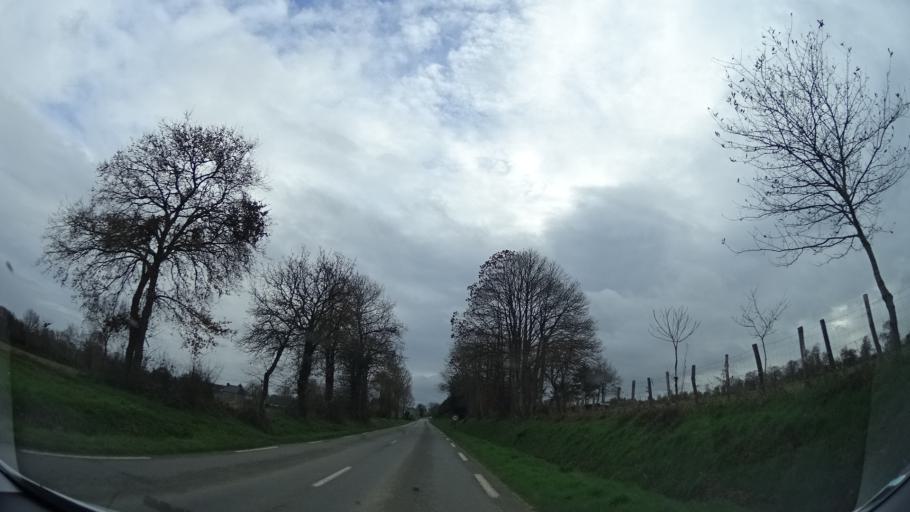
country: FR
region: Brittany
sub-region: Departement des Cotes-d'Armor
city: Evran
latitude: 48.3401
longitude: -1.9654
